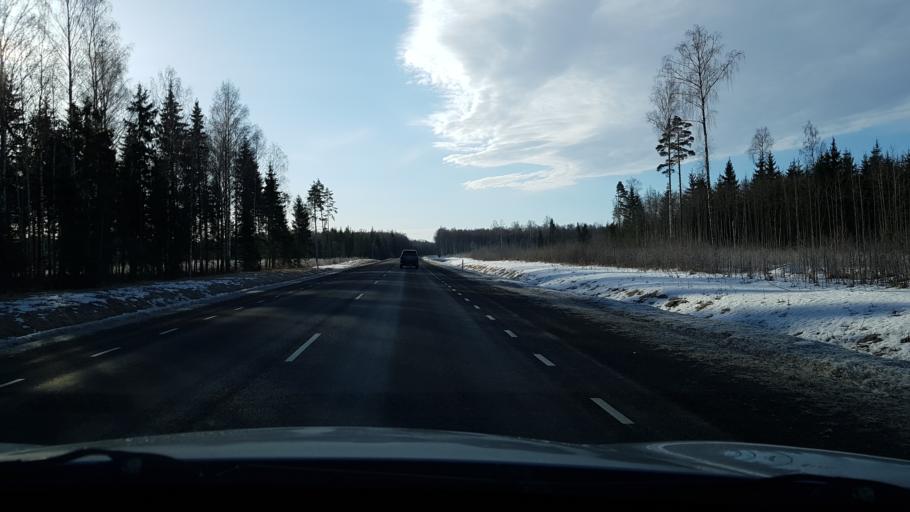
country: EE
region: Viljandimaa
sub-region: Vohma linn
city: Vohma
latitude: 58.6087
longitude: 25.5720
